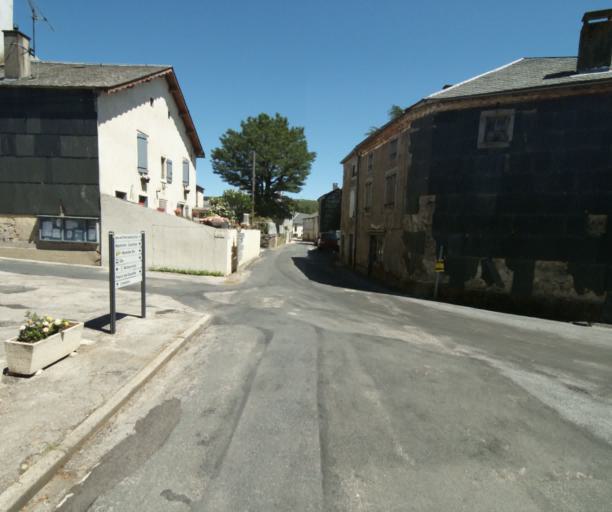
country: FR
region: Midi-Pyrenees
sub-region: Departement du Tarn
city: Dourgne
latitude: 43.4301
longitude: 2.1669
